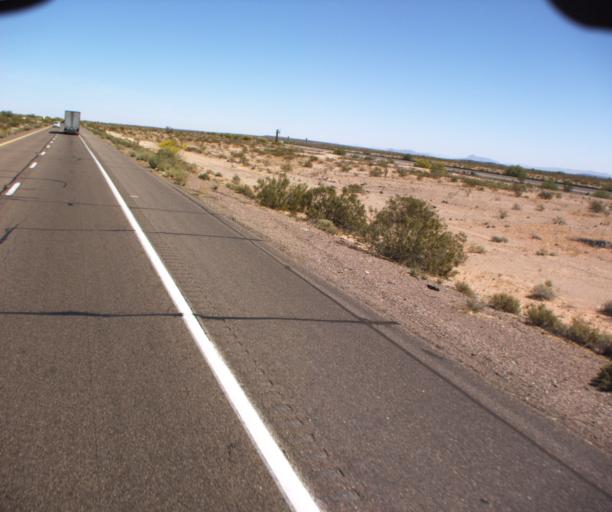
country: US
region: Arizona
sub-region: Maricopa County
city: Gila Bend
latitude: 32.8633
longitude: -113.1659
